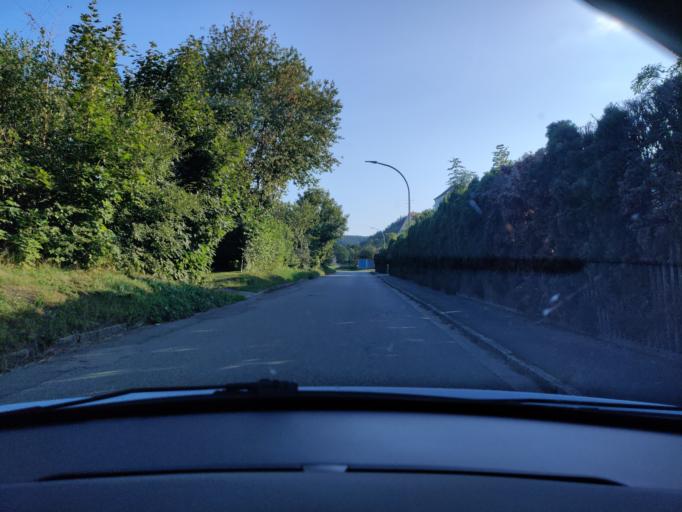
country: DE
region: Bavaria
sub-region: Upper Palatinate
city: Nabburg
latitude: 49.4459
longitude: 12.1780
